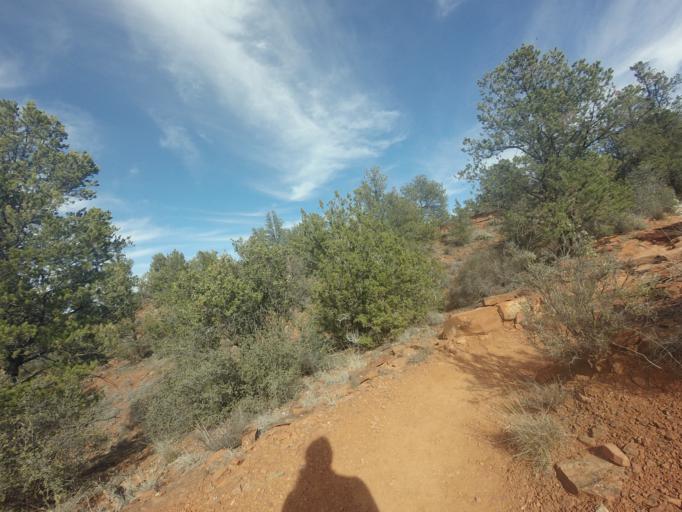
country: US
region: Arizona
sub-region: Yavapai County
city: West Sedona
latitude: 34.8079
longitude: -111.8307
